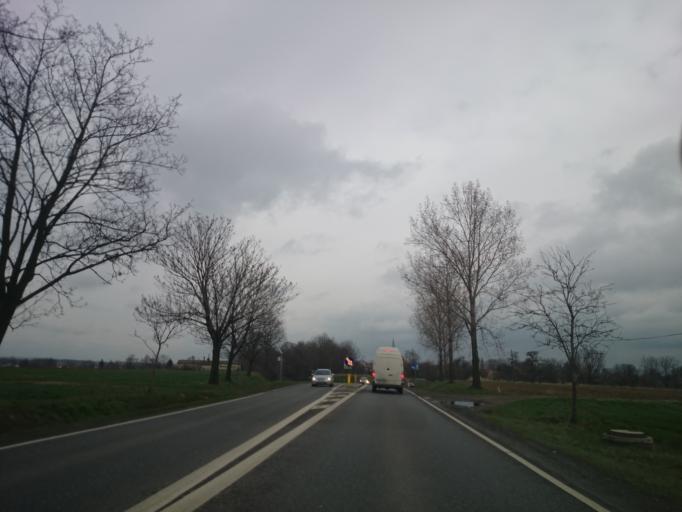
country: PL
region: Opole Voivodeship
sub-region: Powiat nyski
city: Paczkow
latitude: 50.4567
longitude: 17.0374
